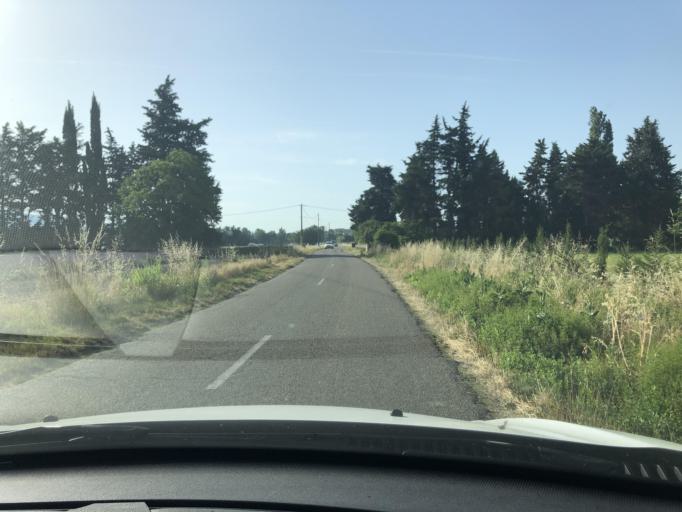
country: FR
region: Provence-Alpes-Cote d'Azur
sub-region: Departement du Vaucluse
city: Velleron
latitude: 43.9646
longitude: 5.0196
